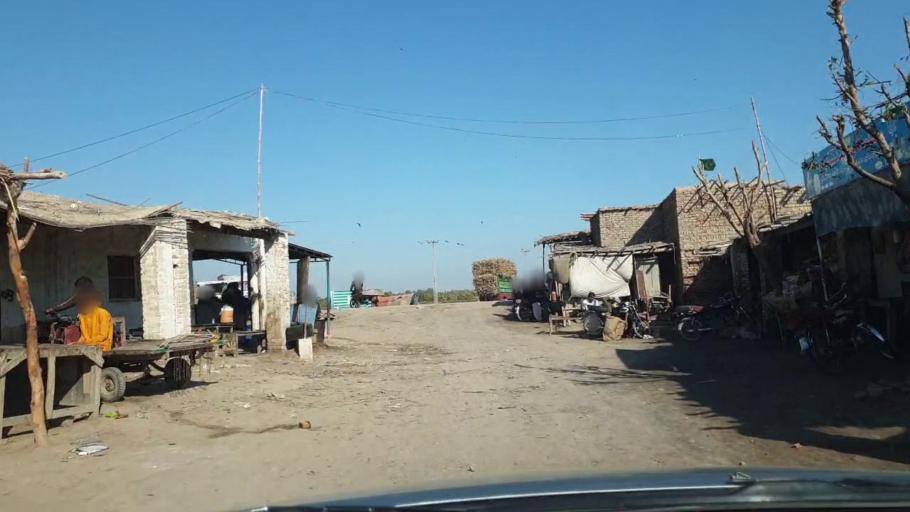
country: PK
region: Sindh
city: Jhol
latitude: 25.9269
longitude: 68.9980
